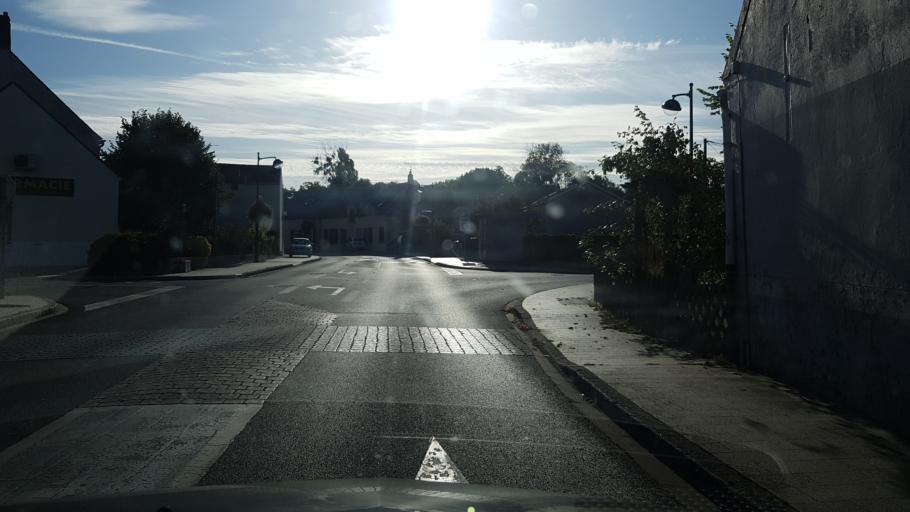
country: FR
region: Centre
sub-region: Departement du Loiret
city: Poilly-lez-Gien
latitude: 47.6781
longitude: 2.5978
